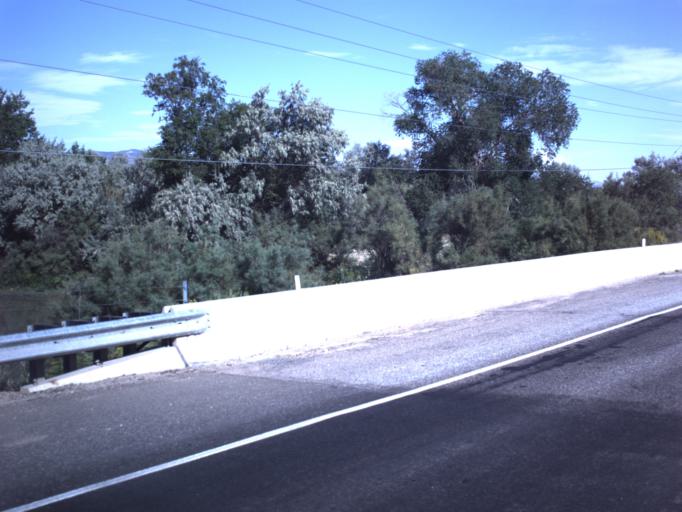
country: US
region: Utah
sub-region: Sevier County
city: Salina
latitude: 38.9914
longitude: -111.8610
